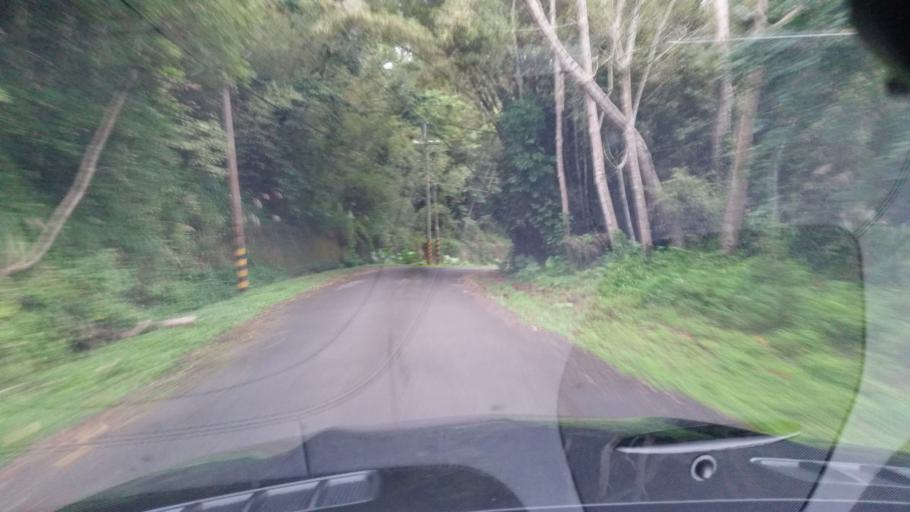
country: TW
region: Taiwan
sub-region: Miaoli
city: Miaoli
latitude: 24.5863
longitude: 120.8977
